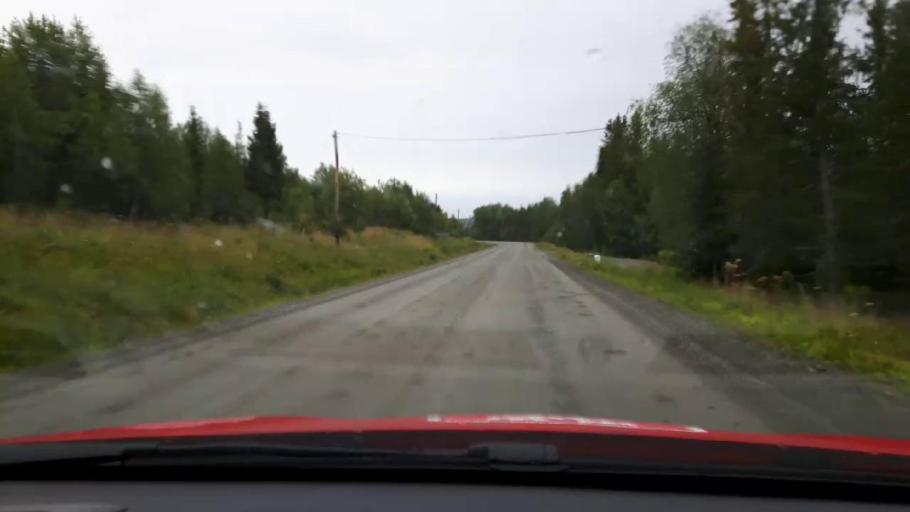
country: SE
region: Jaemtland
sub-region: Are Kommun
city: Are
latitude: 63.4559
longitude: 12.6440
